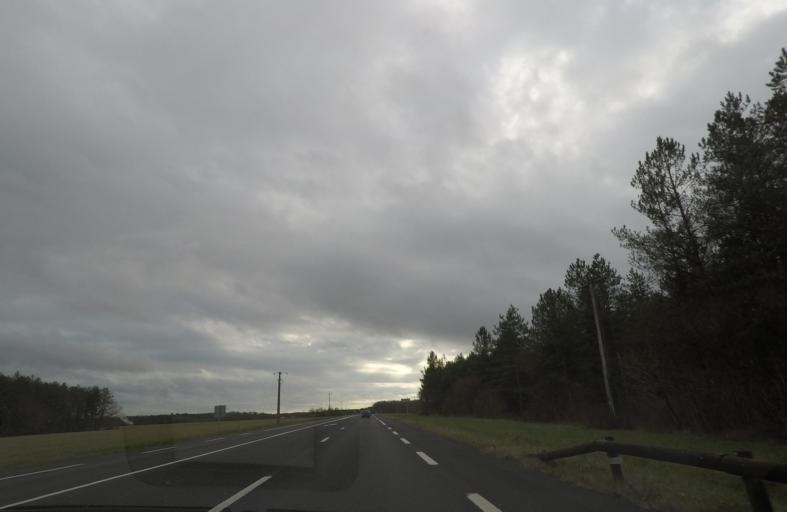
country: FR
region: Centre
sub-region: Departement du Loir-et-Cher
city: Soings-en-Sologne
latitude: 47.4493
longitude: 1.5359
